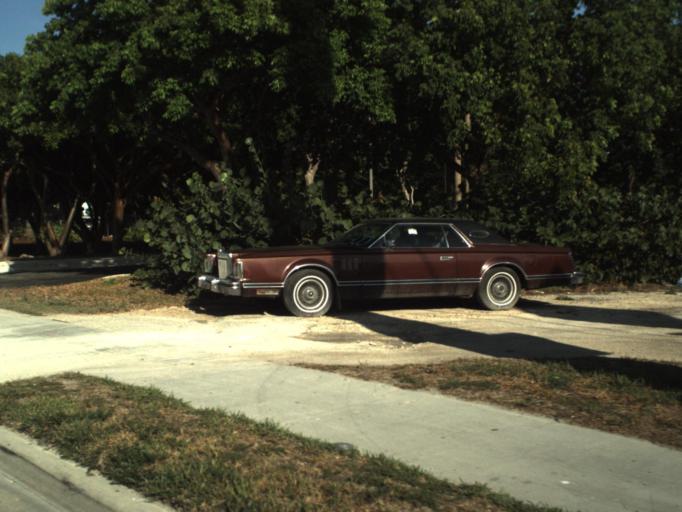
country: US
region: Florida
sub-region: Monroe County
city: Marathon
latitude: 24.7185
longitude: -81.0666
